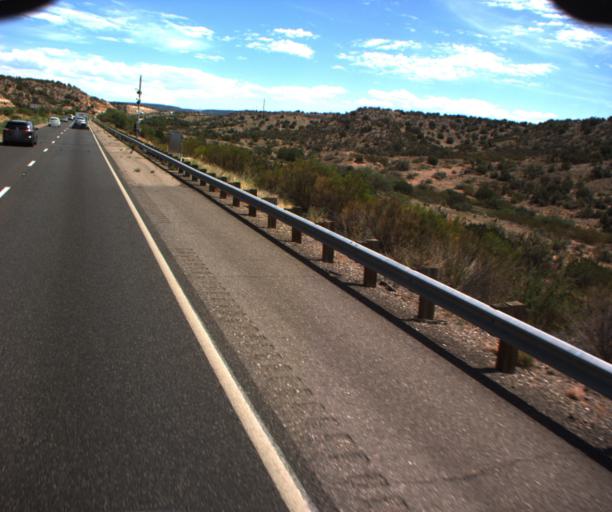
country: US
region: Arizona
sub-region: Yavapai County
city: Lake Montezuma
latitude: 34.6631
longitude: -111.7854
